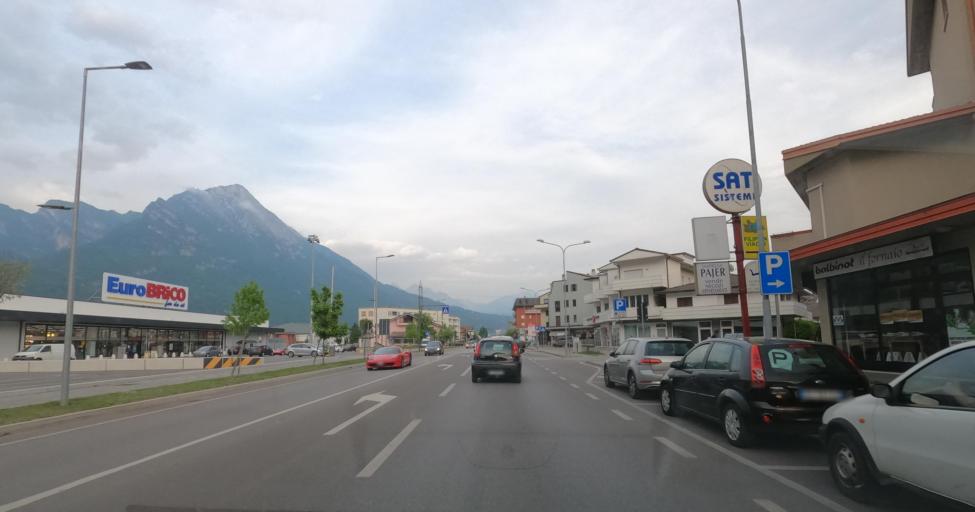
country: IT
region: Veneto
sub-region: Provincia di Belluno
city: Ponte nell'Alpi
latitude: 46.1808
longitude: 12.2768
